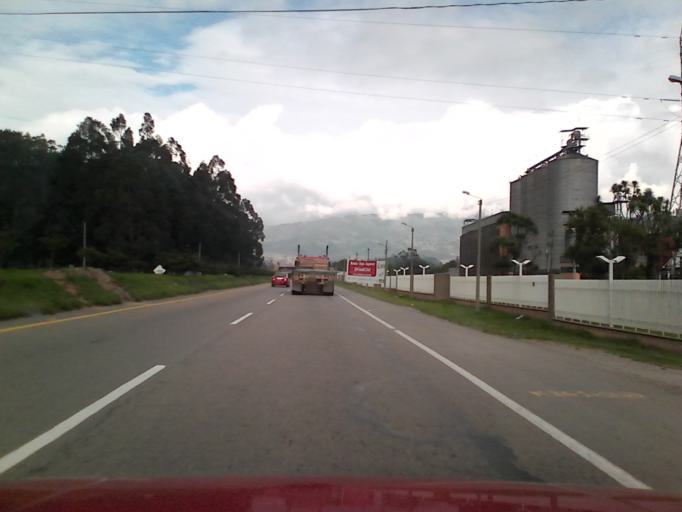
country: CO
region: Boyaca
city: Duitama
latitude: 5.8023
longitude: -73.0041
